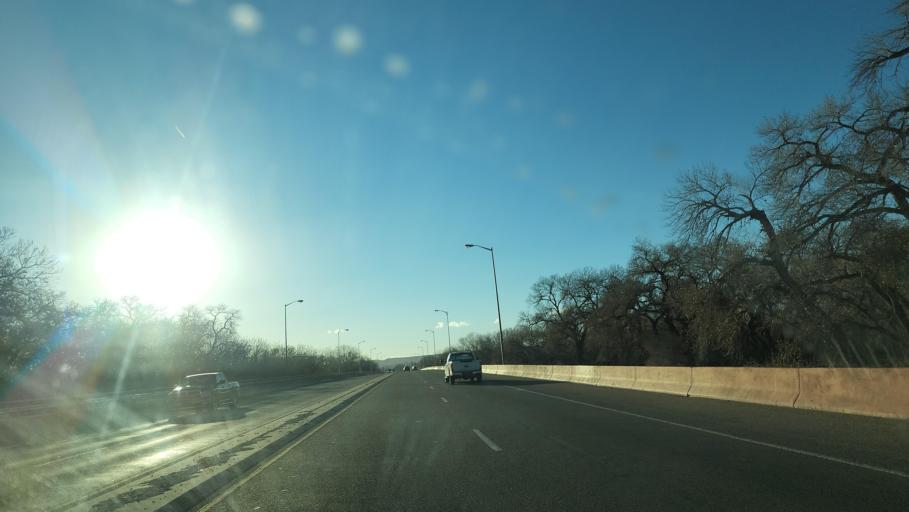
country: US
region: New Mexico
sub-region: Bernalillo County
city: South Valley
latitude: 35.0272
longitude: -106.6695
